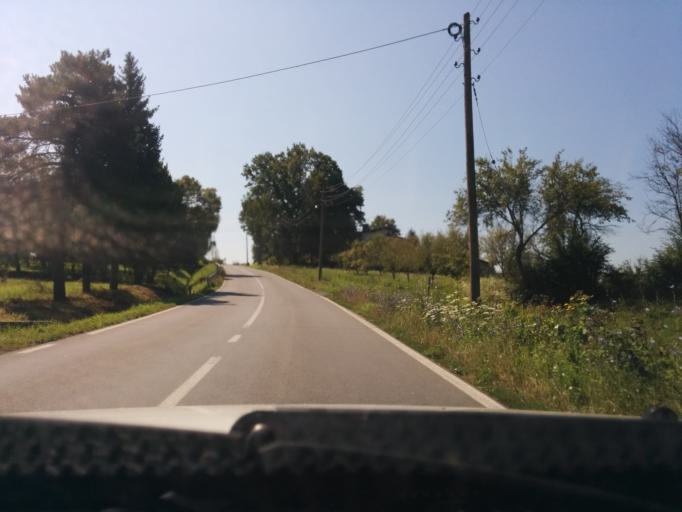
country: HR
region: Sisacko-Moslavacka
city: Lipovljani
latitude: 45.4163
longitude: 16.9018
